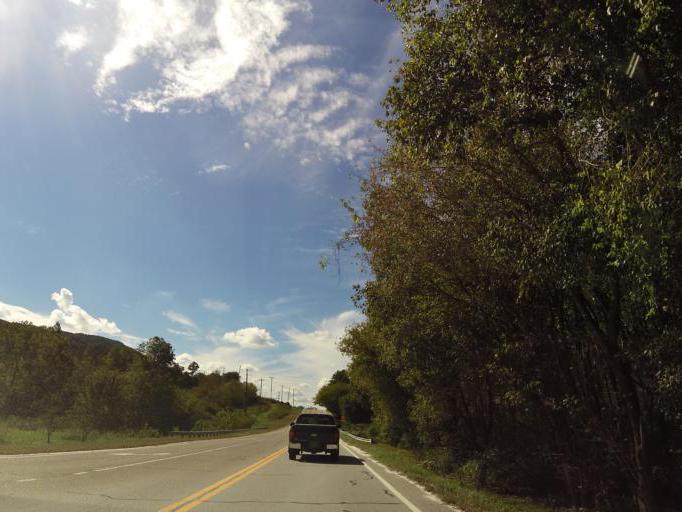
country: US
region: Georgia
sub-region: Pickens County
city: Nelson
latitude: 34.4350
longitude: -84.3453
